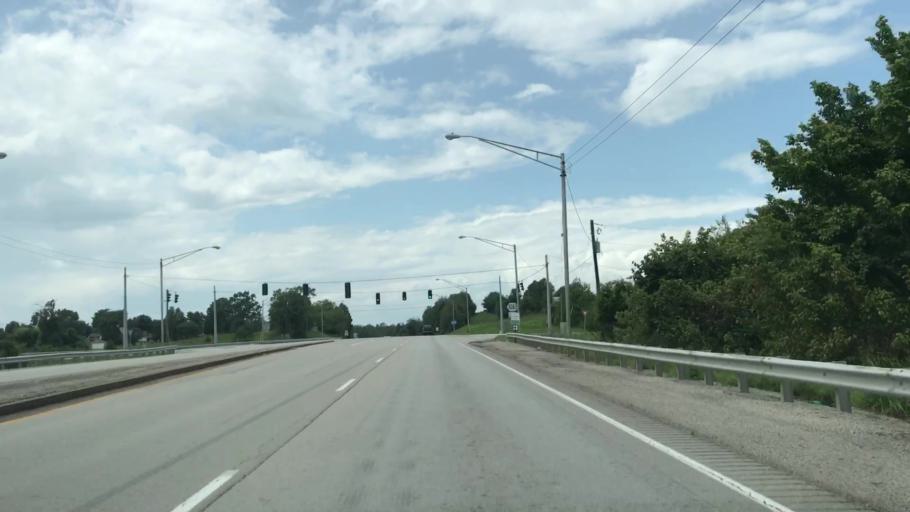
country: US
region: Kentucky
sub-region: Pulaski County
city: Somerset
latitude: 37.0935
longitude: -84.6289
